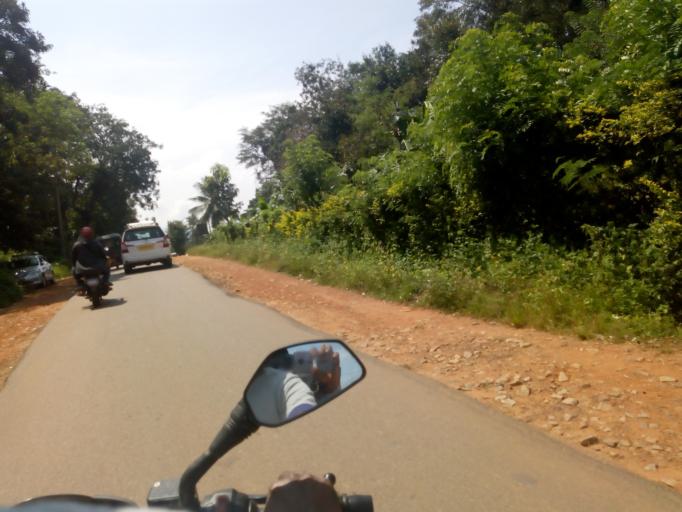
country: IN
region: Karnataka
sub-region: Kodagu
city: Ponnampet
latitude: 12.0339
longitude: 75.9718
